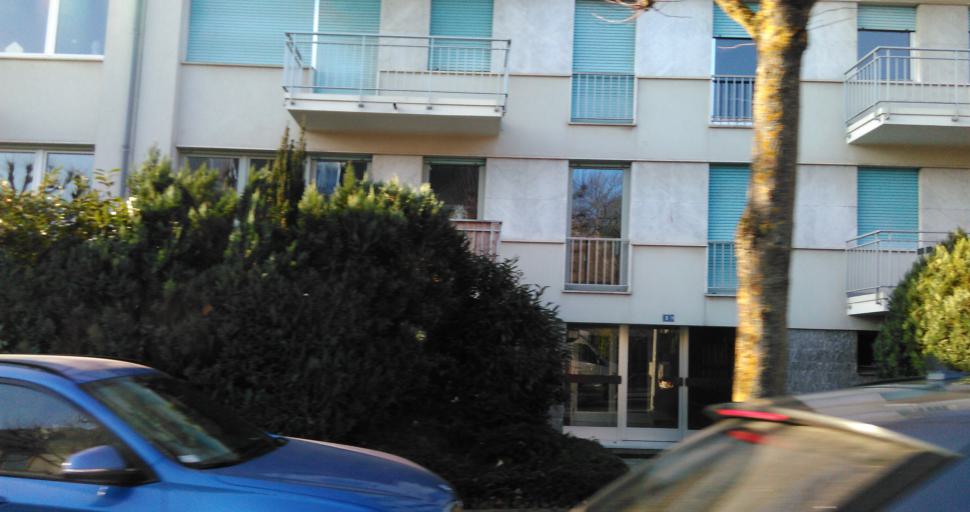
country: LU
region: Luxembourg
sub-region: Canton de Luxembourg
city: Luxembourg
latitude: 49.6091
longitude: 6.1209
